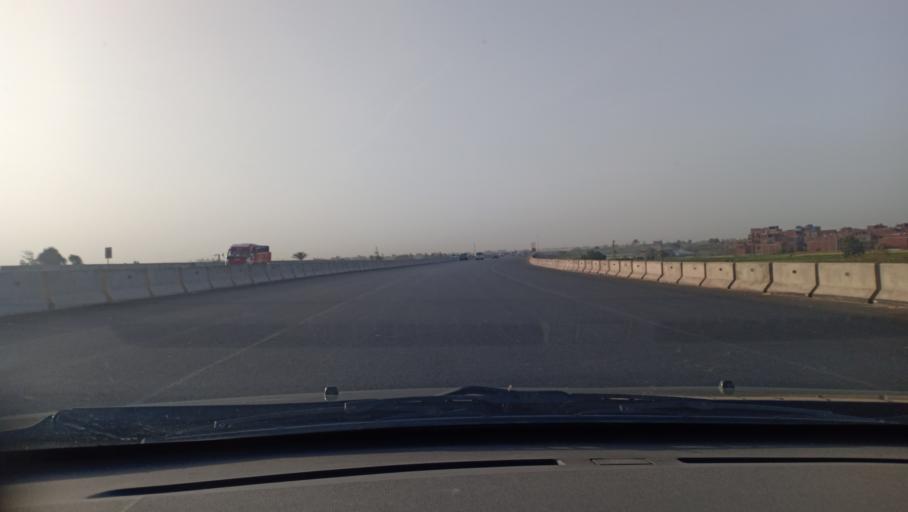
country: EG
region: Muhafazat al Qalyubiyah
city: Qalyub
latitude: 30.1818
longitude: 31.2437
